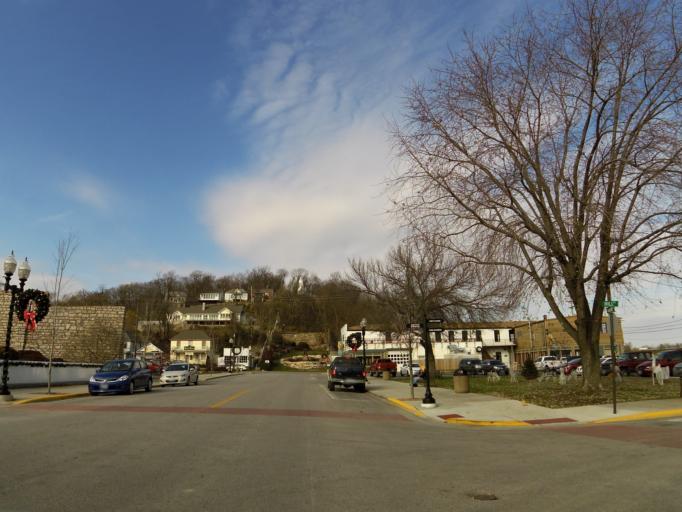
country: US
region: Missouri
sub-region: Marion County
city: Hannibal
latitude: 39.7120
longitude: -91.3574
